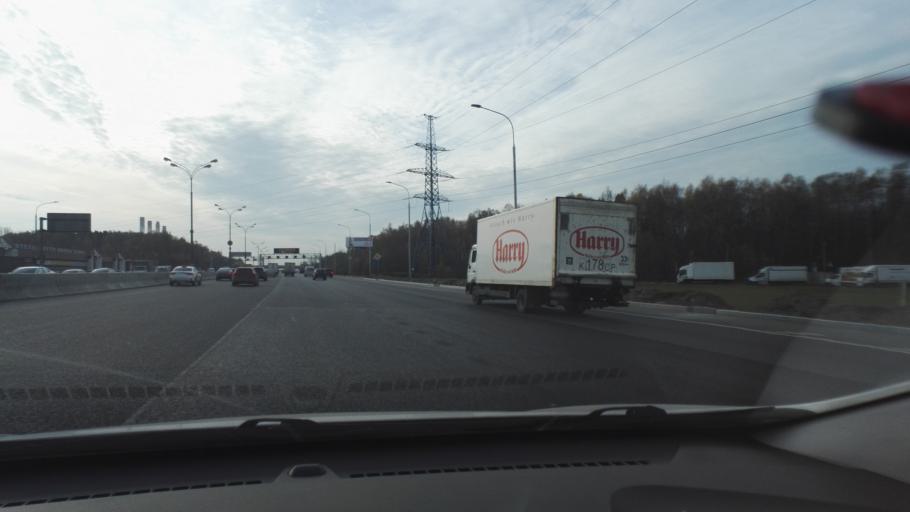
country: RU
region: Moscow
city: Vagonoremont
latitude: 55.9042
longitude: 37.5224
